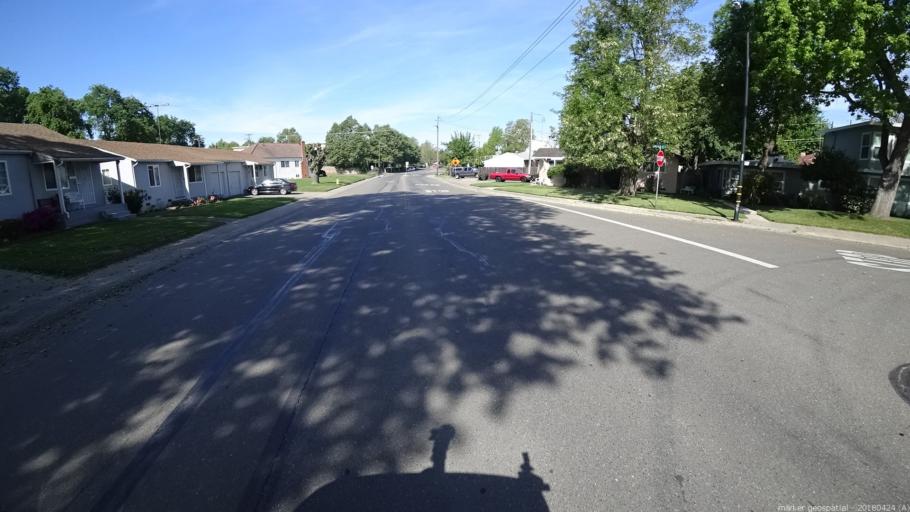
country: US
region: California
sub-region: Yolo County
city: West Sacramento
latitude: 38.5631
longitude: -121.5361
